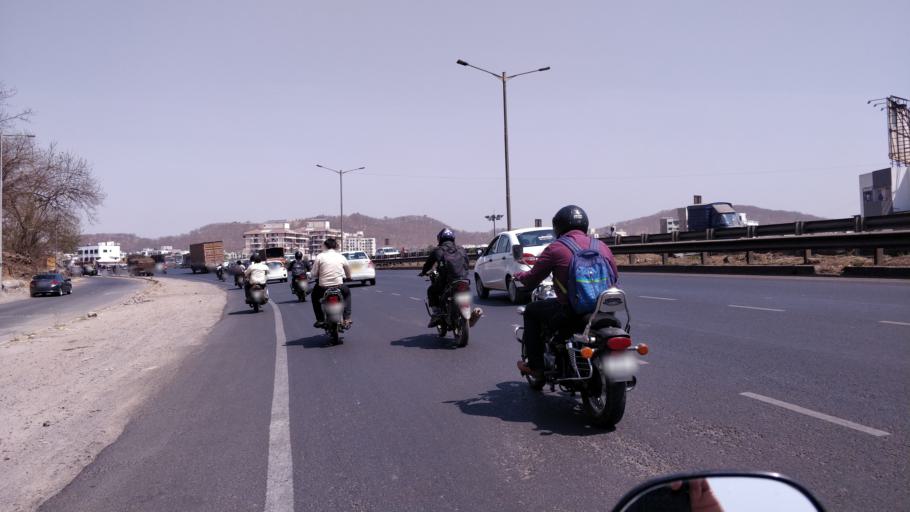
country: IN
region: Maharashtra
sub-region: Pune Division
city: Shivaji Nagar
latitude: 18.5382
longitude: 73.7811
